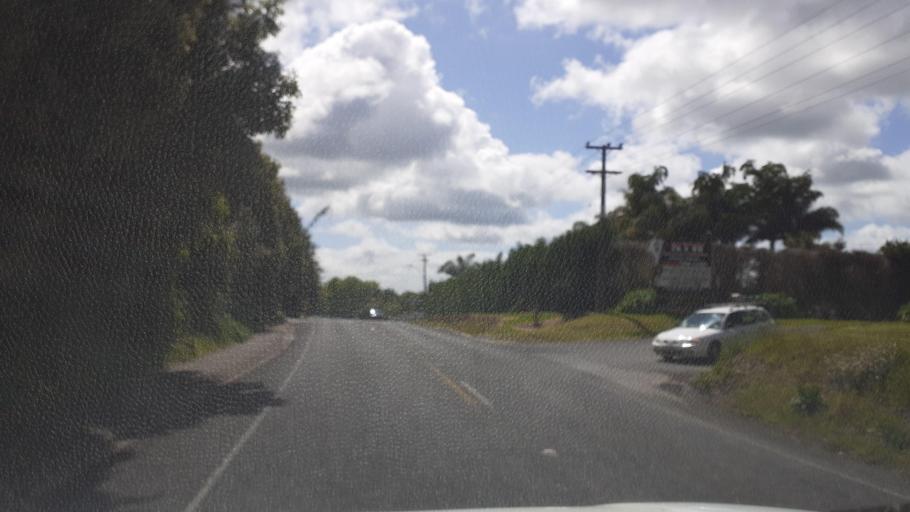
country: NZ
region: Northland
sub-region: Far North District
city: Kerikeri
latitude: -35.2229
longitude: 173.9750
